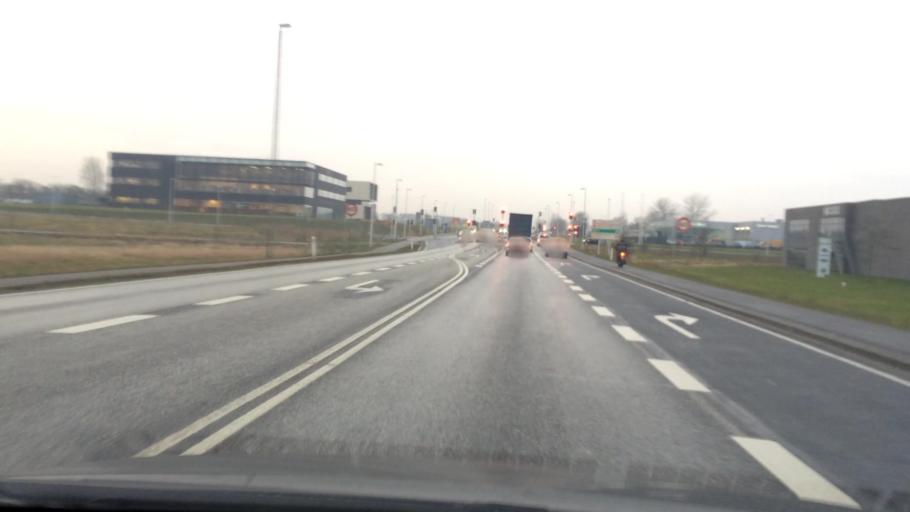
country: DK
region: Central Jutland
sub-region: Horsens Kommune
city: Horsens
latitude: 55.8327
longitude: 9.8062
